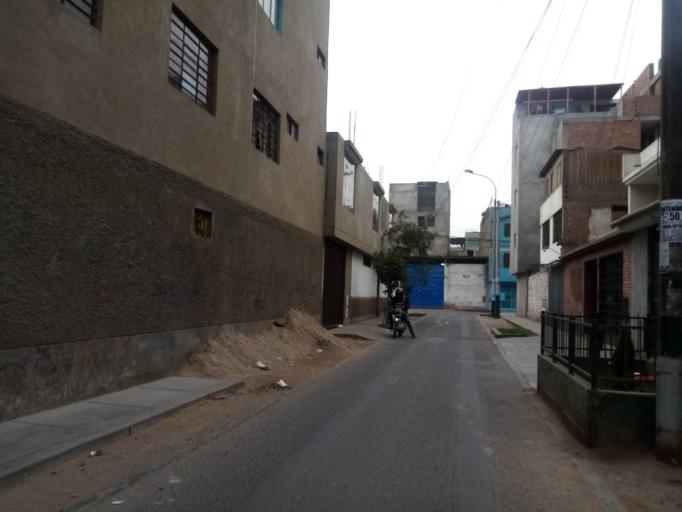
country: PE
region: Lima
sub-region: Lima
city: Vitarte
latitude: -12.0443
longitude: -76.9570
